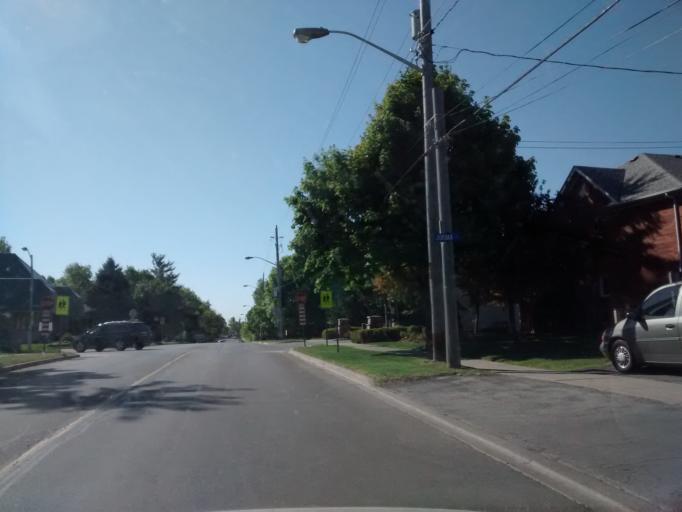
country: CA
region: Ontario
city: Burlington
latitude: 43.3785
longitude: -79.8162
